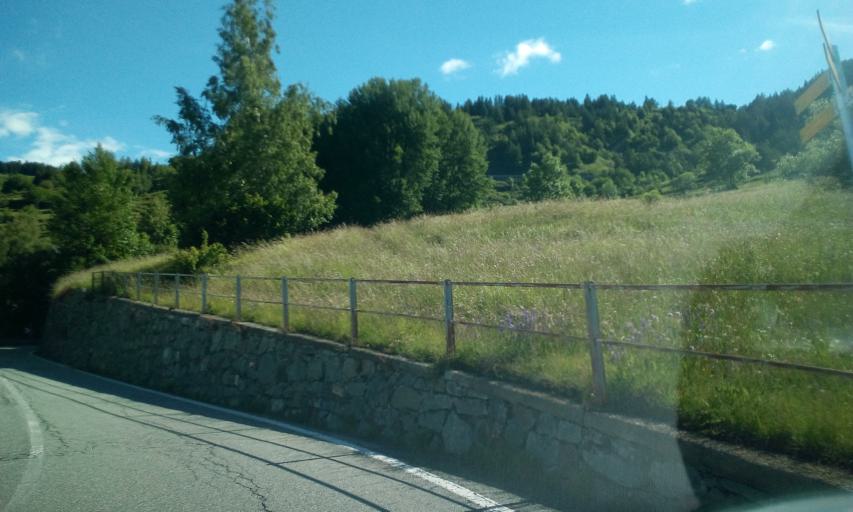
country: IT
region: Aosta Valley
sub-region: Valle d'Aosta
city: Emarese
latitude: 45.7496
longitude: 7.6877
